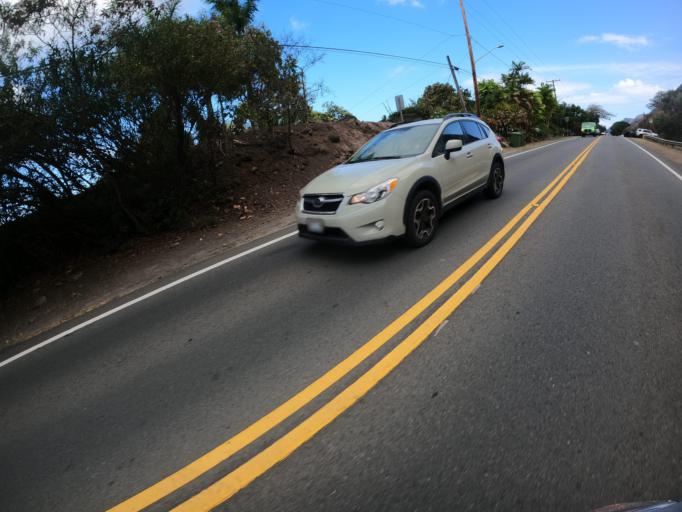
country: US
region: Hawaii
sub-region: Honolulu County
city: Waimanalo Beach
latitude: 21.3240
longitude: -157.6795
